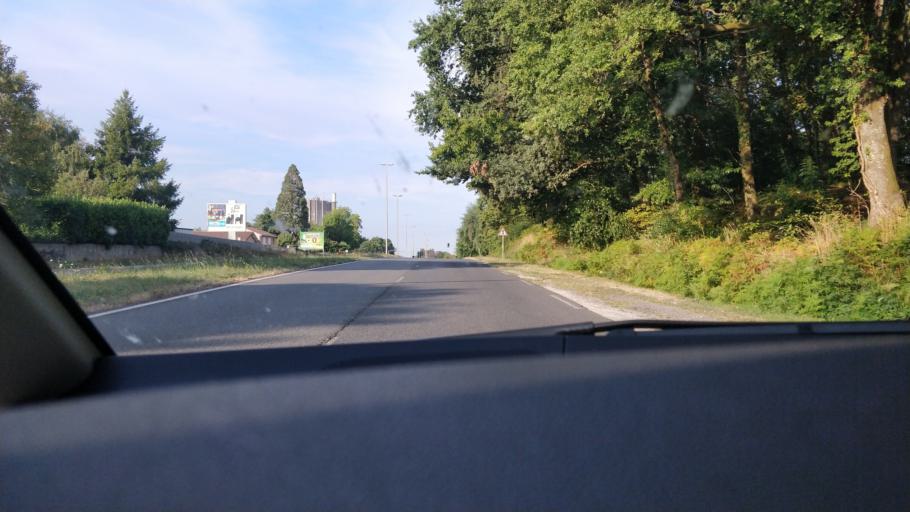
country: FR
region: Limousin
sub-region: Departement de la Haute-Vienne
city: Le Palais-sur-Vienne
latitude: 45.8673
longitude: 1.2944
